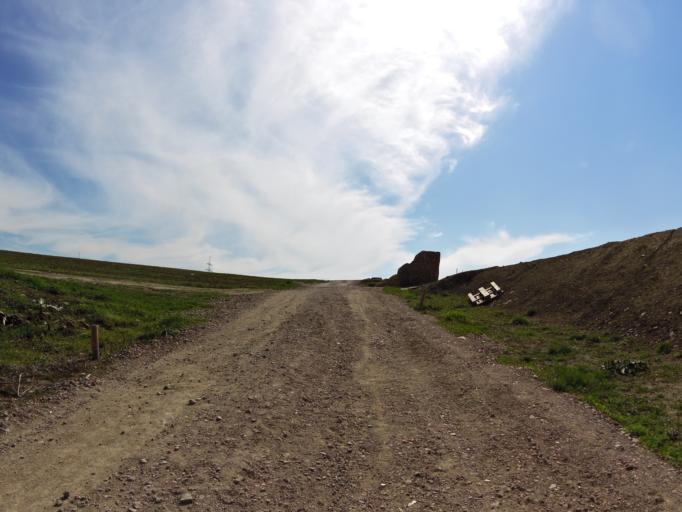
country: DE
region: Bavaria
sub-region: Regierungsbezirk Unterfranken
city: Rottendorf
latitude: 49.7883
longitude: 10.0390
